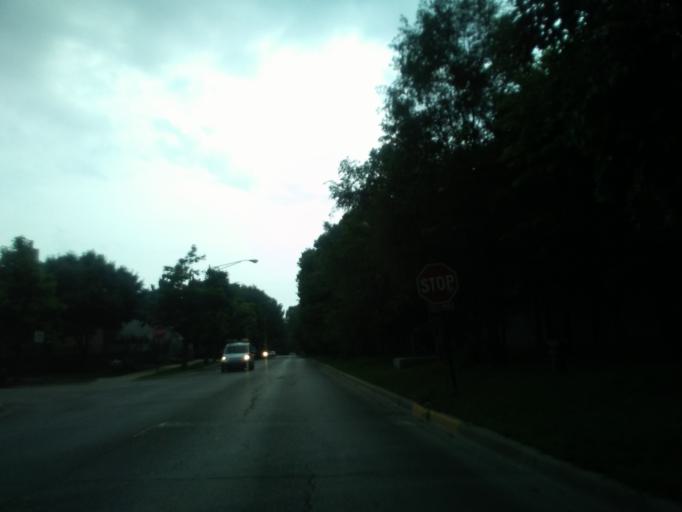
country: US
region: Illinois
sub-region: Cook County
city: Lincolnwood
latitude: 41.9809
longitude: -87.6819
